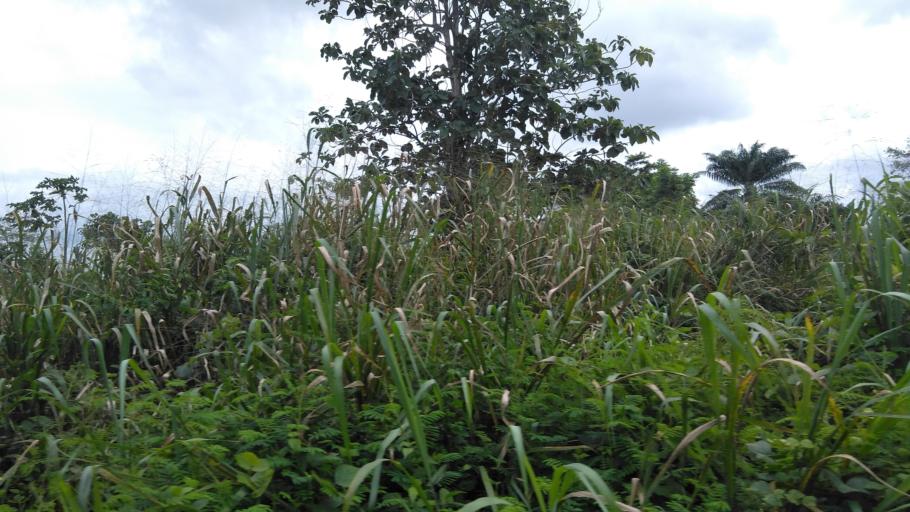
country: NG
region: Ogun
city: Abigi
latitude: 6.5940
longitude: 4.4978
